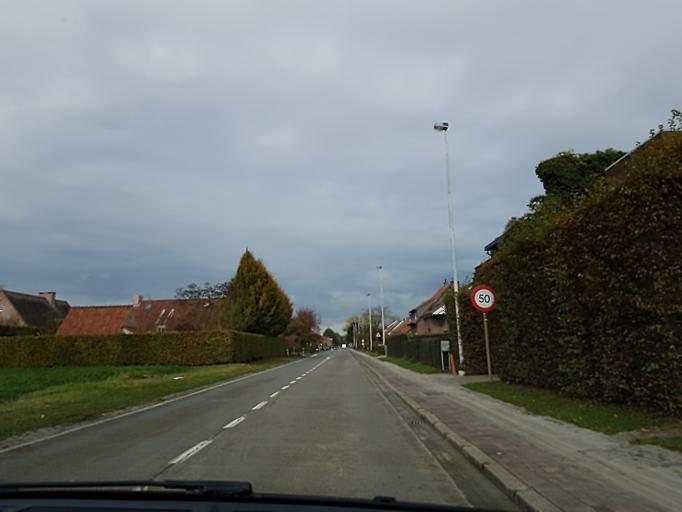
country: BE
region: Flanders
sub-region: Provincie Antwerpen
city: Boechout
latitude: 51.1427
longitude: 4.4885
